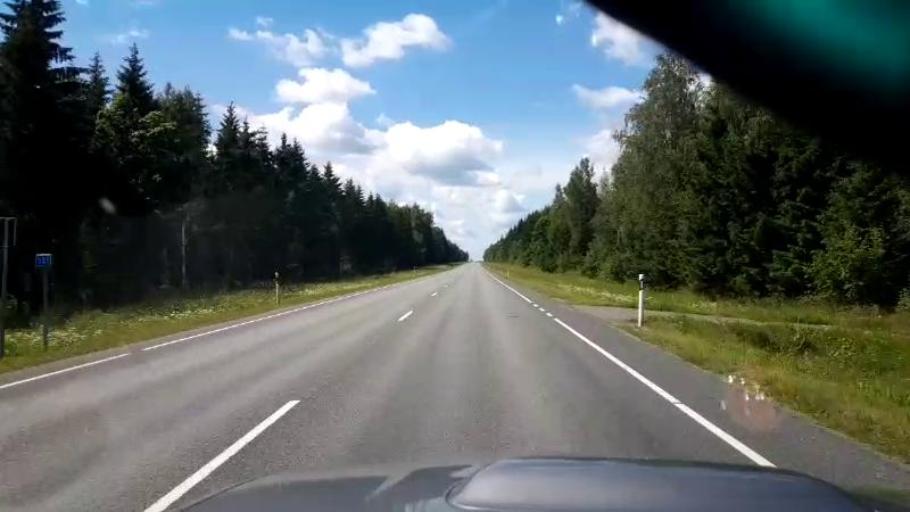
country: EE
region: Jaervamaa
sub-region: Jaerva-Jaani vald
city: Jarva-Jaani
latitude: 59.1868
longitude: 25.8028
